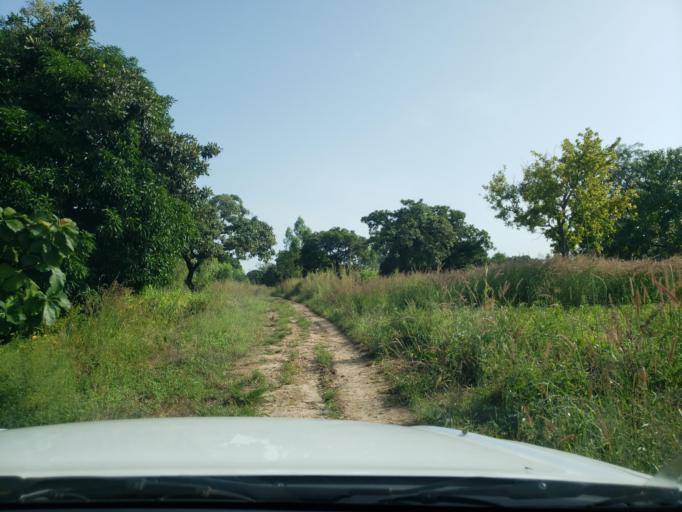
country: TG
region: Kara
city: Bafilo
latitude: 9.4096
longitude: 1.1760
